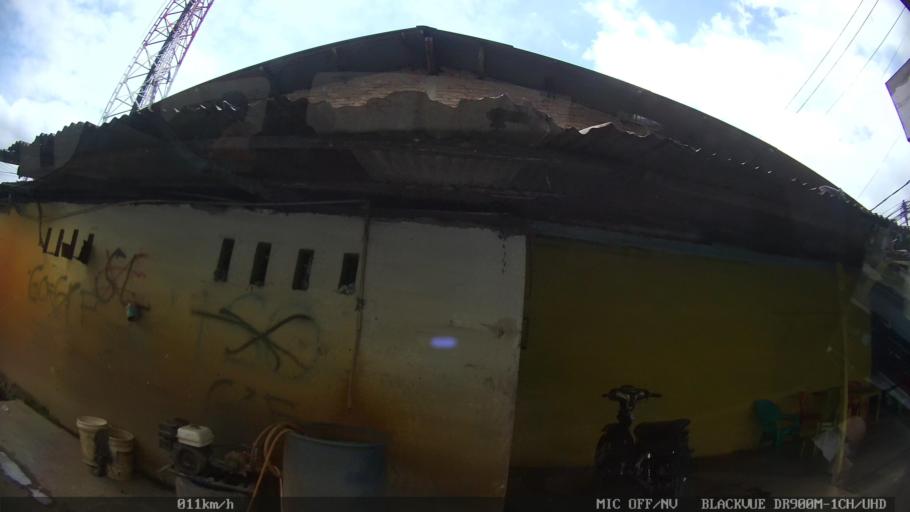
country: ID
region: North Sumatra
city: Sunggal
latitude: 3.6058
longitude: 98.6236
